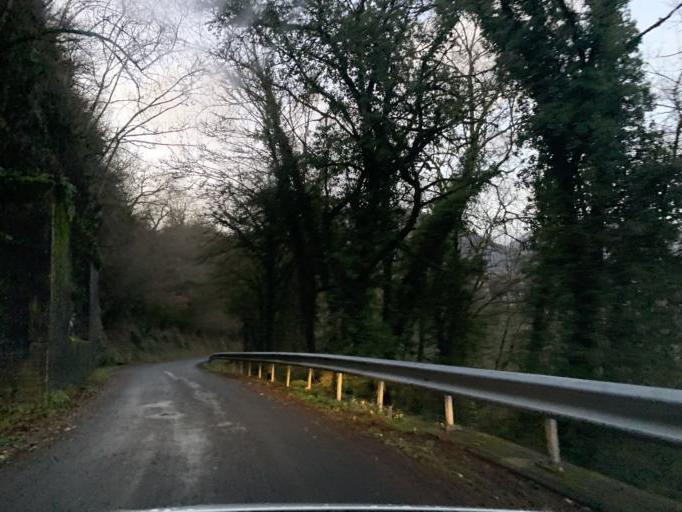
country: FR
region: Rhone-Alpes
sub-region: Departement de l'Ain
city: Virieu-le-Grand
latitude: 45.8118
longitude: 5.6582
